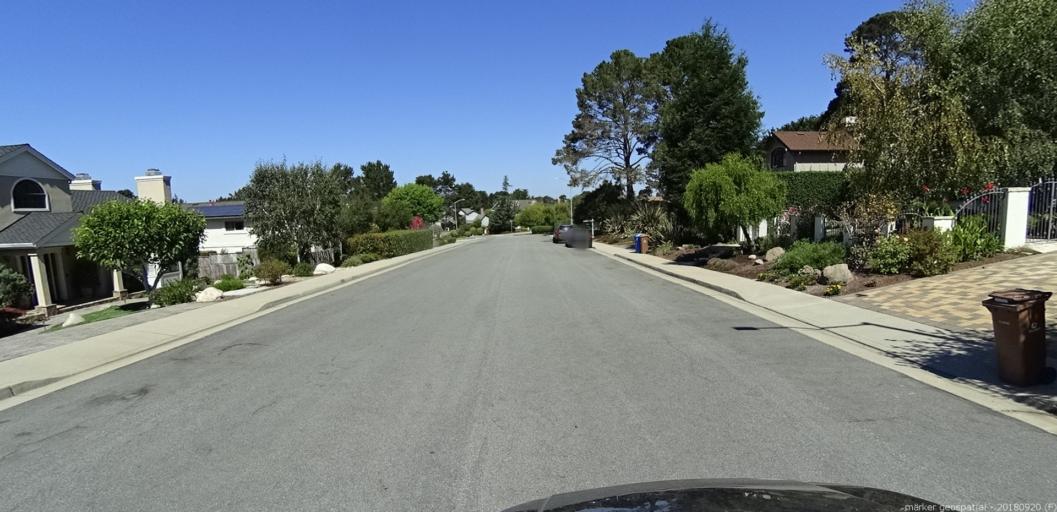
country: US
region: California
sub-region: Monterey County
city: Del Rey Oaks
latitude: 36.5759
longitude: -121.8614
